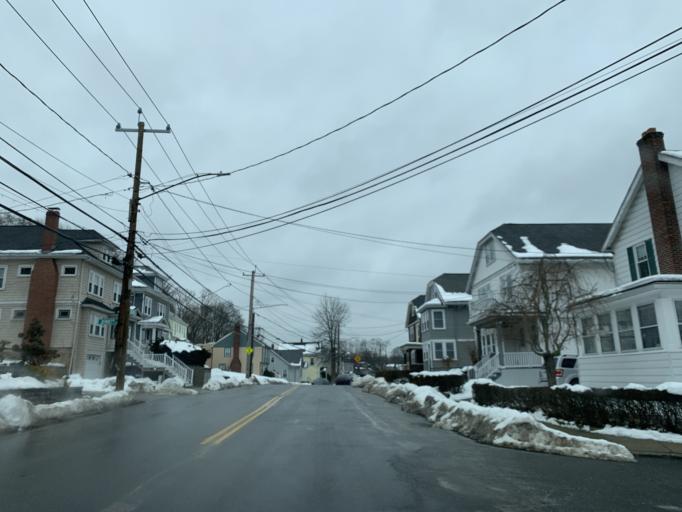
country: US
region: Massachusetts
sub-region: Norfolk County
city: Dedham
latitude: 42.2845
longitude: -71.1623
